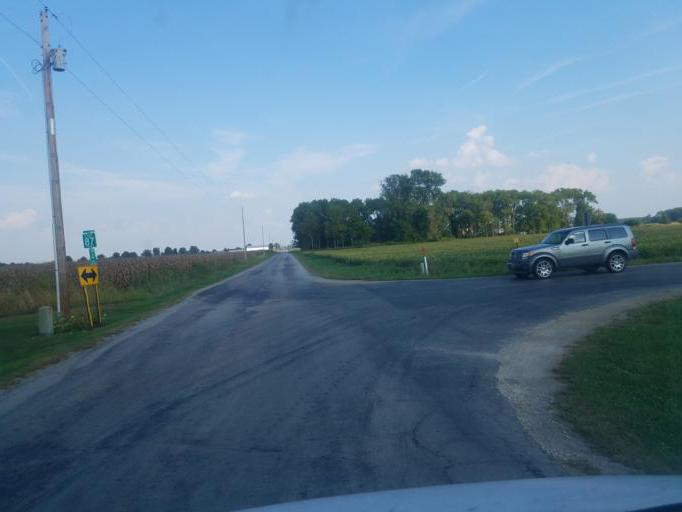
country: US
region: Ohio
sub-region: Wyandot County
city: Carey
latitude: 40.9050
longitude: -83.4625
